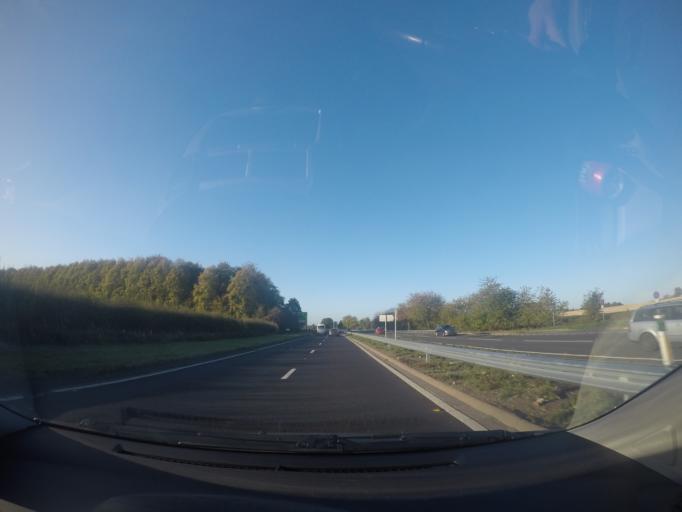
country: GB
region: England
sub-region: City of York
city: Askham Richard
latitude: 53.9150
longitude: -1.1752
